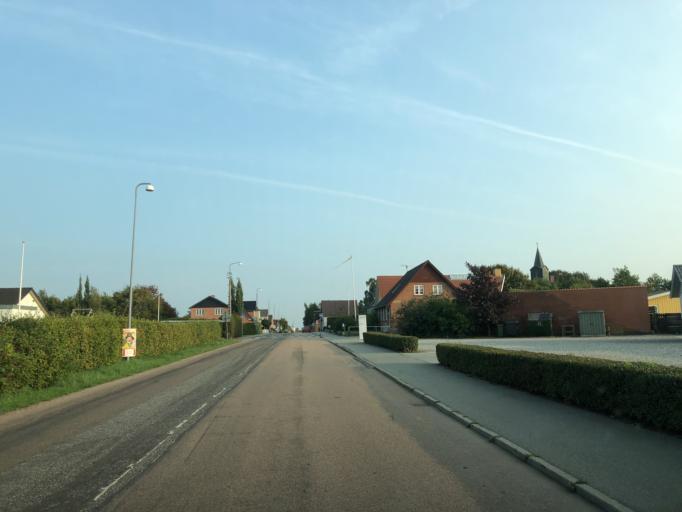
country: DK
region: South Denmark
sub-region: Vejle Kommune
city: Jelling
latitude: 55.7111
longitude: 9.3740
